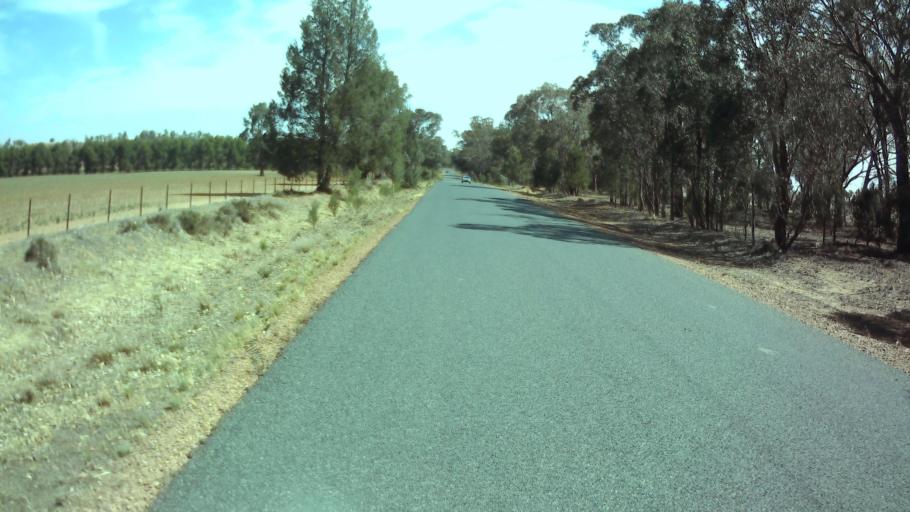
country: AU
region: New South Wales
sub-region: Weddin
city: Grenfell
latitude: -34.0402
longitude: 148.1340
